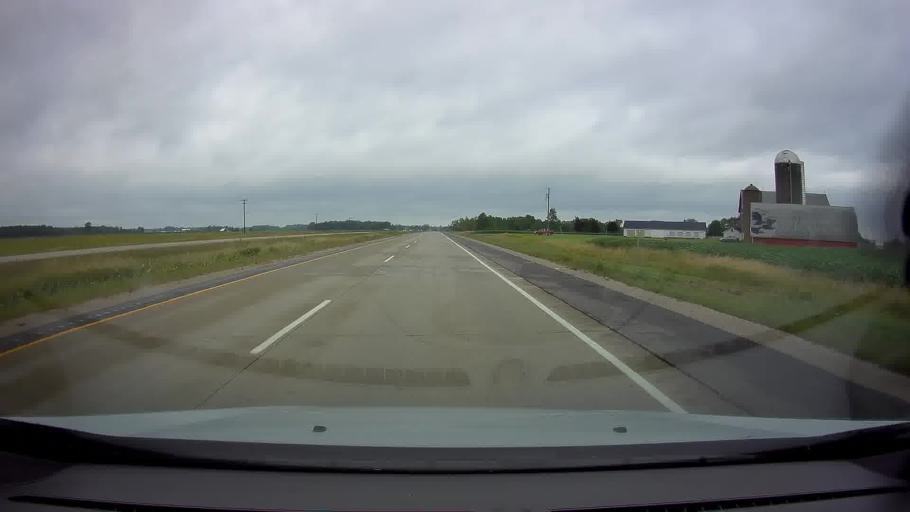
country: US
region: Wisconsin
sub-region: Brown County
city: Pulaski
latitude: 44.6075
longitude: -88.2553
